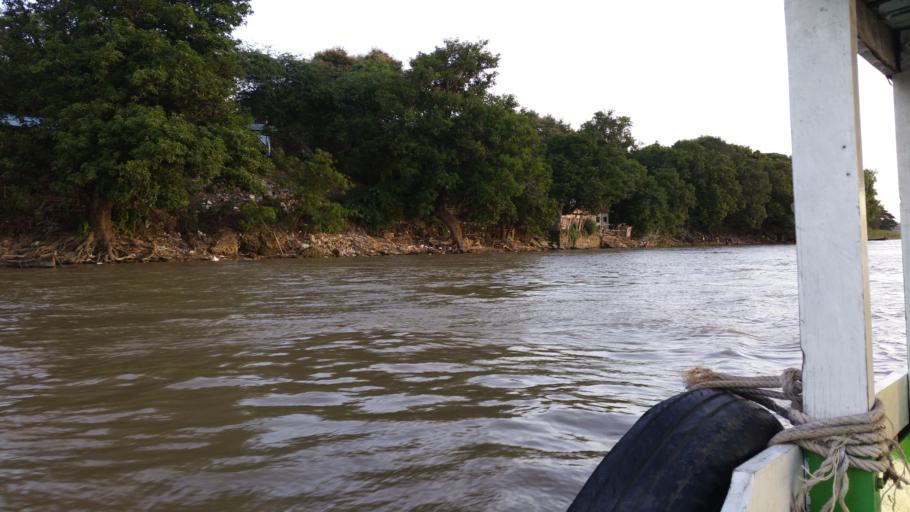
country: MM
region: Magway
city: Pakokku
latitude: 21.1966
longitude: 94.8914
